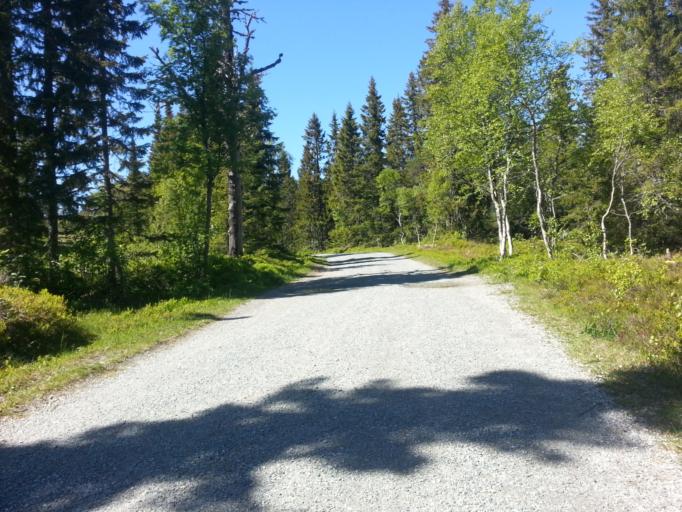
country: NO
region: Sor-Trondelag
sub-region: Trondheim
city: Trondheim
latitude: 63.4118
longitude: 10.2833
